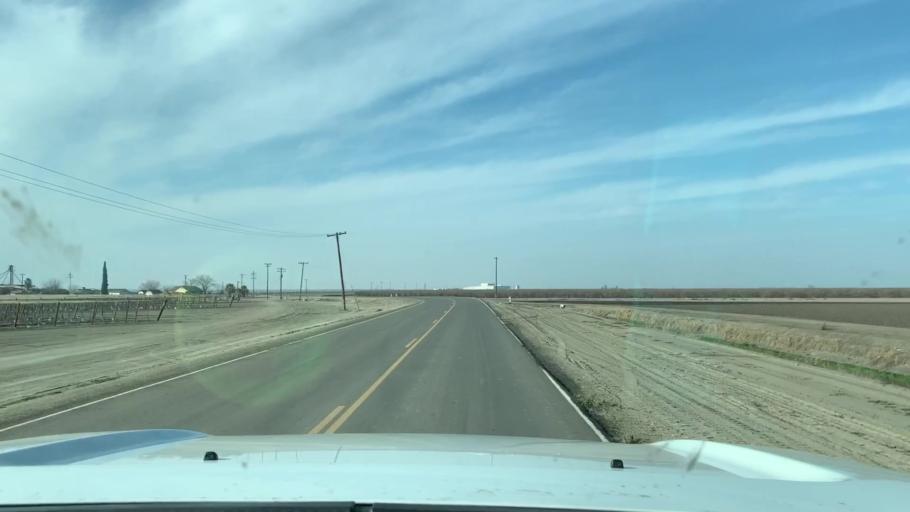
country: US
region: California
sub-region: Kern County
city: Buttonwillow
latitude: 35.4835
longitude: -119.5927
